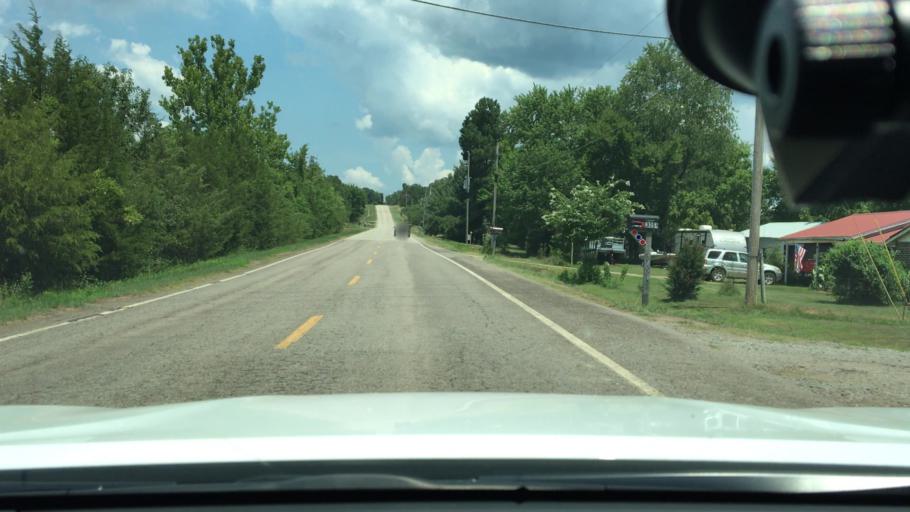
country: US
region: Arkansas
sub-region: Logan County
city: Booneville
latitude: 35.1515
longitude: -93.8770
